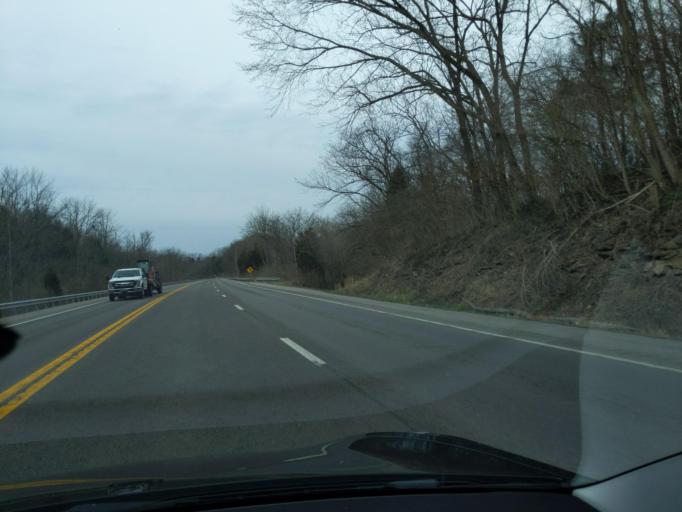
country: US
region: Kentucky
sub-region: Clark County
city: Winchester
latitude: 37.8916
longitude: -84.2788
